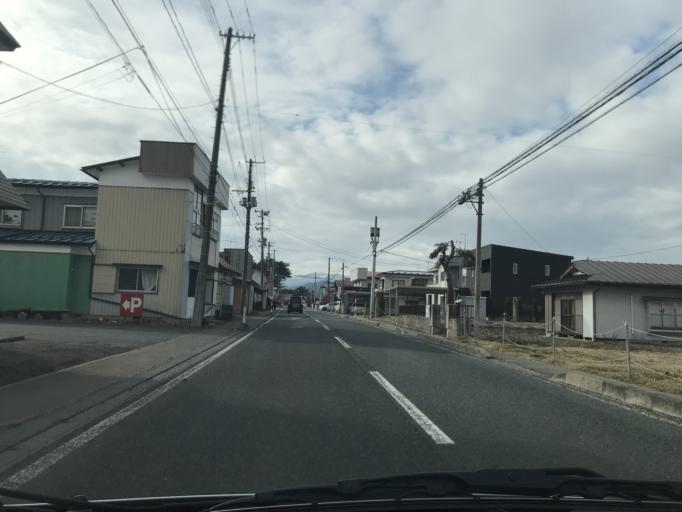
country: JP
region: Iwate
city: Hanamaki
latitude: 39.4092
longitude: 141.1017
